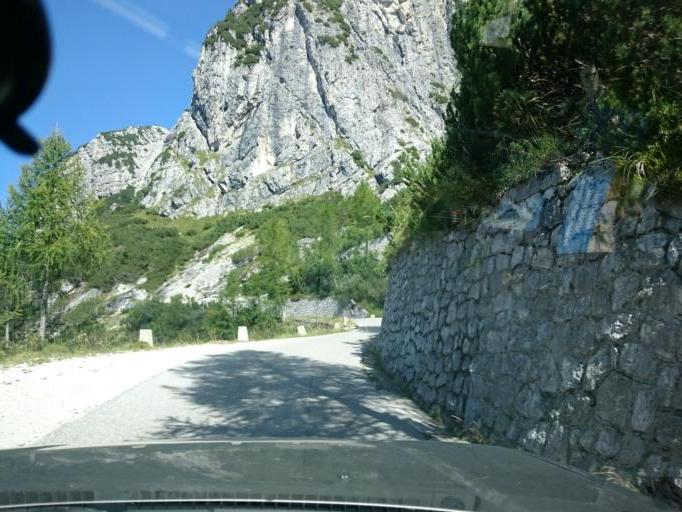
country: IT
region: Friuli Venezia Giulia
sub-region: Provincia di Udine
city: Tarvisio
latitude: 46.4376
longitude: 13.6270
